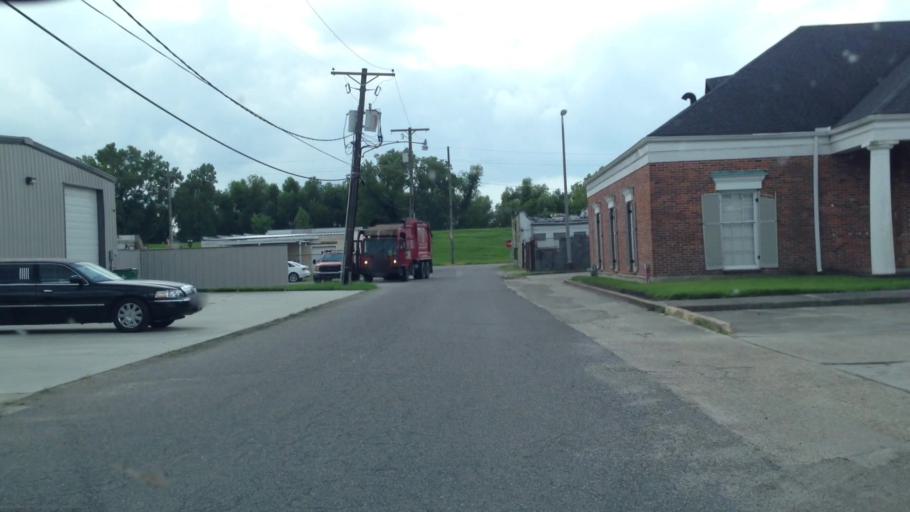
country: US
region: Louisiana
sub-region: Saint Charles Parish
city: Norco
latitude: 29.9976
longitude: -90.4127
